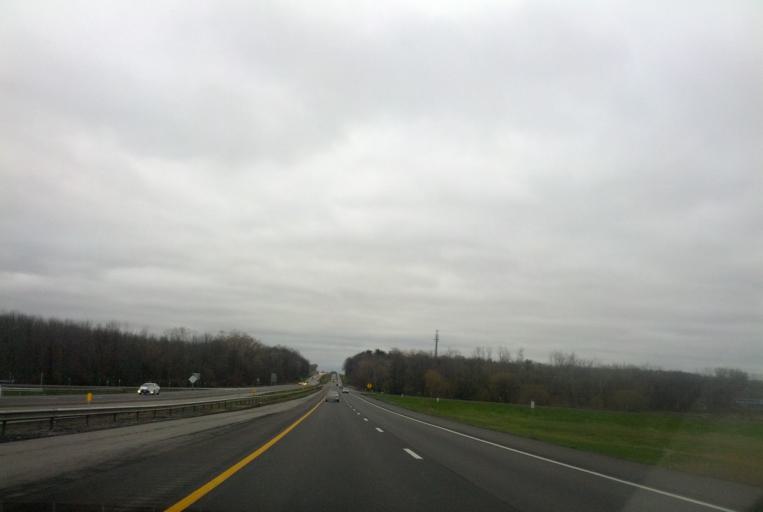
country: US
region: New York
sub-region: Ontario County
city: Phelps
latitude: 42.9551
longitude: -76.9830
